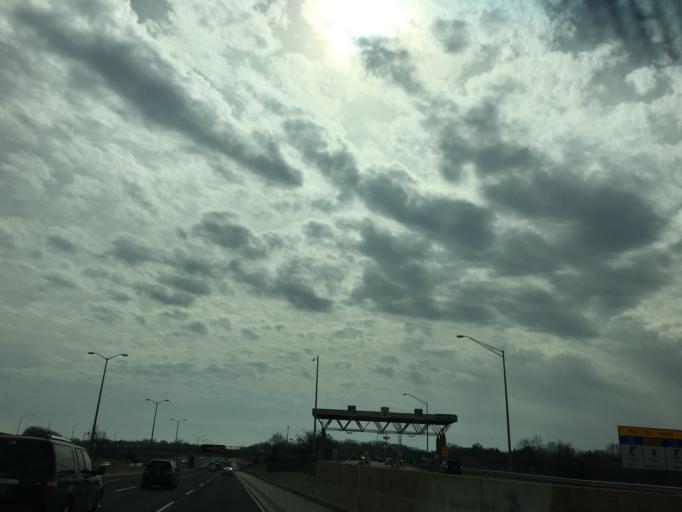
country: US
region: Illinois
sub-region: DuPage County
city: Woodridge
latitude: 41.7743
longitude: -88.0480
